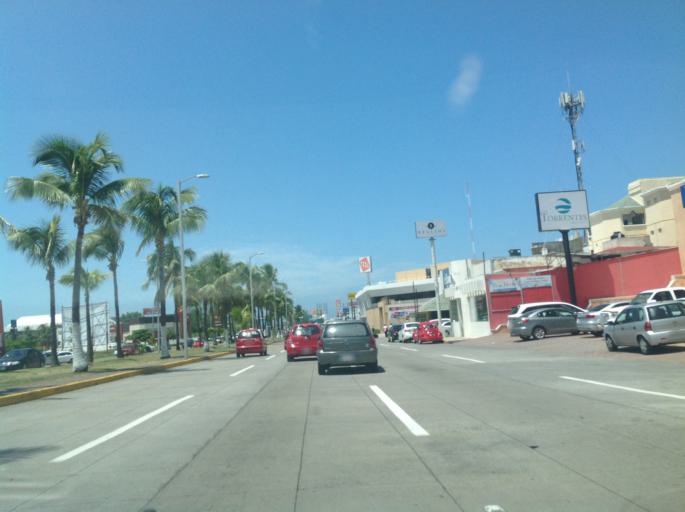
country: MX
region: Veracruz
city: Veracruz
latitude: 19.1574
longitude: -96.1088
